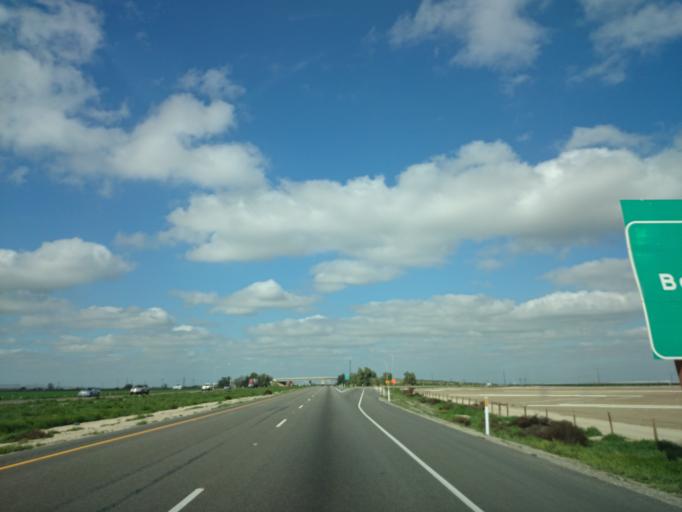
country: US
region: California
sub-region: Kern County
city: Greenfield
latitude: 35.2054
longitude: -119.1587
